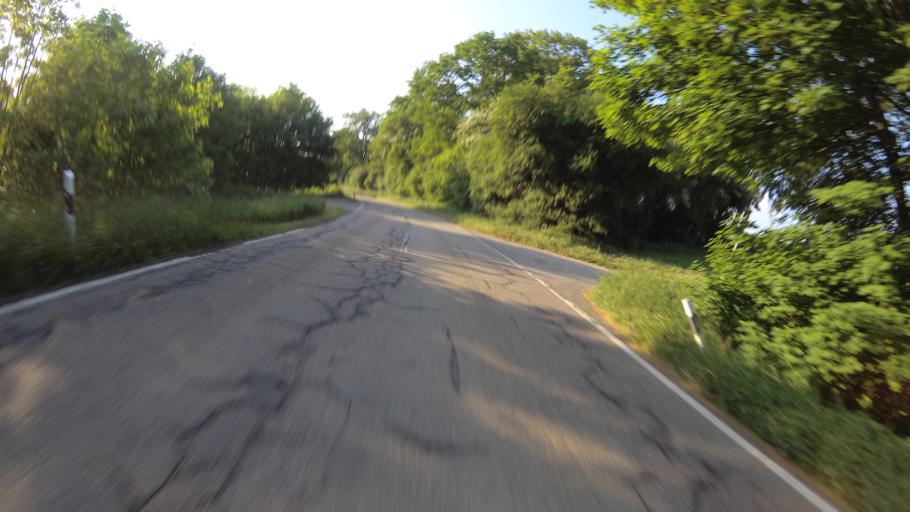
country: DE
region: Rheinland-Pfalz
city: Contwig
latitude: 49.2235
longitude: 7.4165
